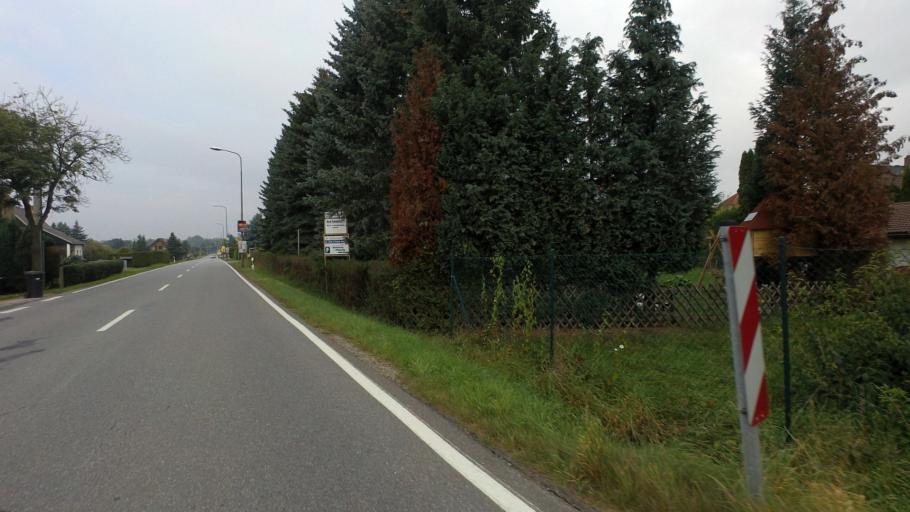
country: DE
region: Saxony
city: Arnsdorf
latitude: 51.0871
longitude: 14.0162
